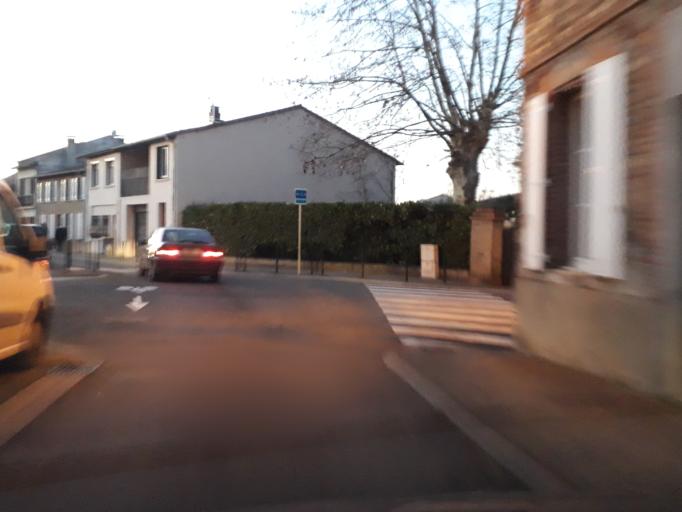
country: FR
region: Midi-Pyrenees
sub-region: Departement de la Haute-Garonne
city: Carbonne
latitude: 43.2967
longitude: 1.2229
